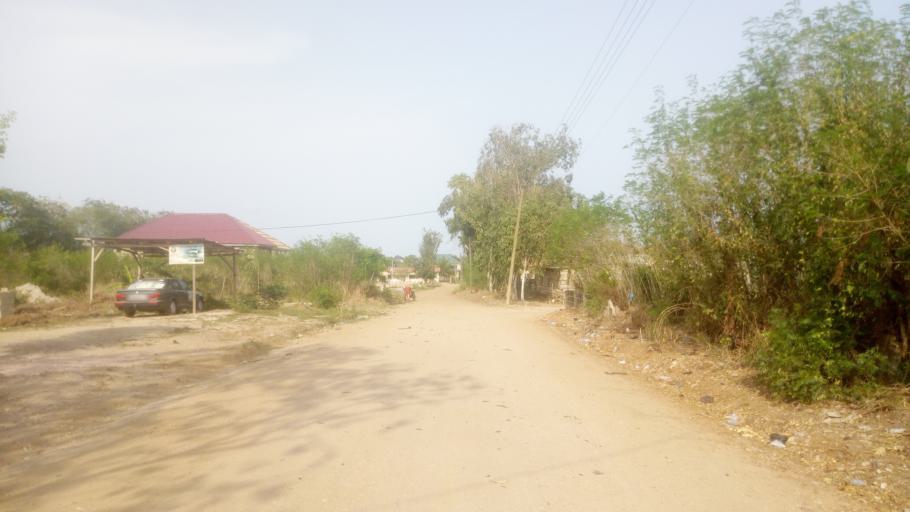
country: GH
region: Central
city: Winneba
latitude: 5.3784
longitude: -0.6401
